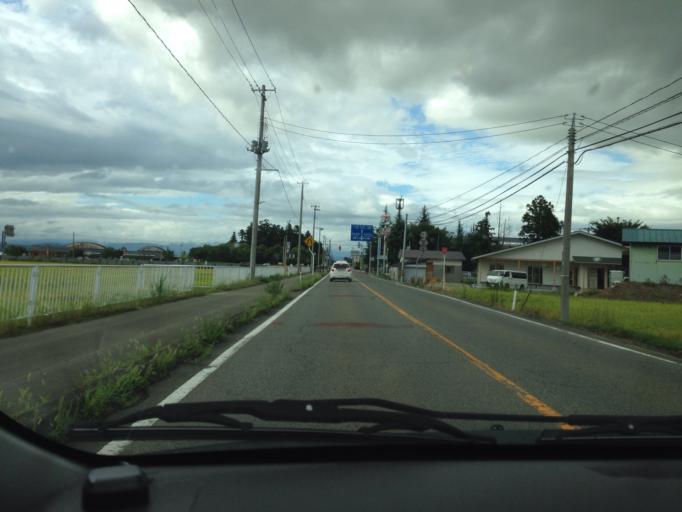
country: JP
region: Fukushima
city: Kitakata
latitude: 37.4949
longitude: 139.8720
